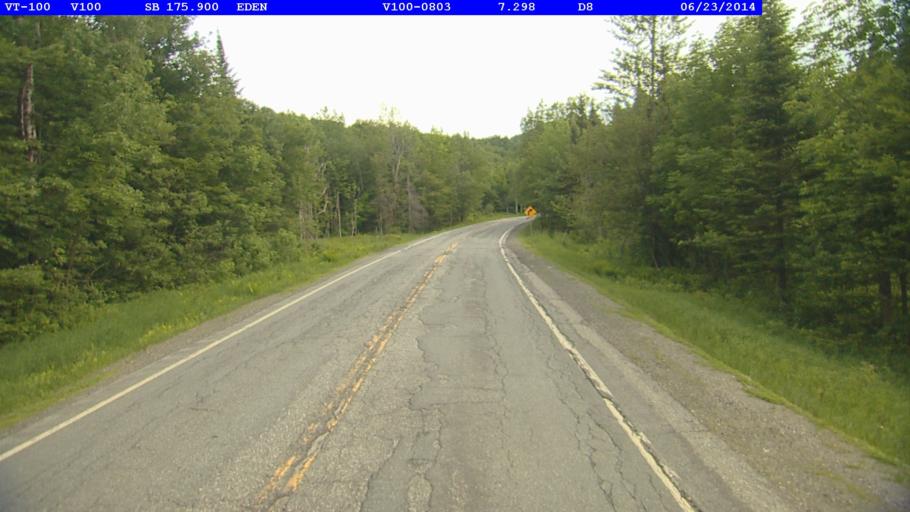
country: US
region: Vermont
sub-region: Lamoille County
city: Hyde Park
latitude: 44.7355
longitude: -72.4705
